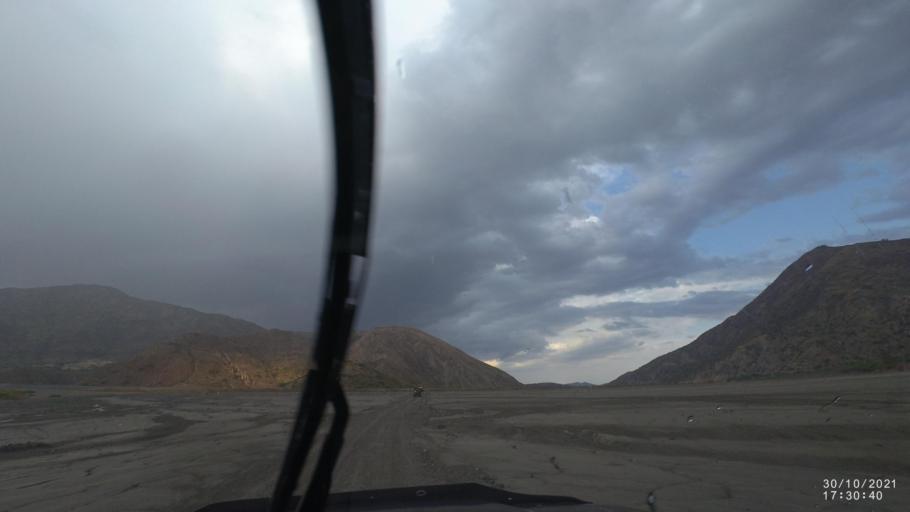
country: BO
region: Cochabamba
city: Sipe Sipe
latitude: -17.5238
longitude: -66.5967
